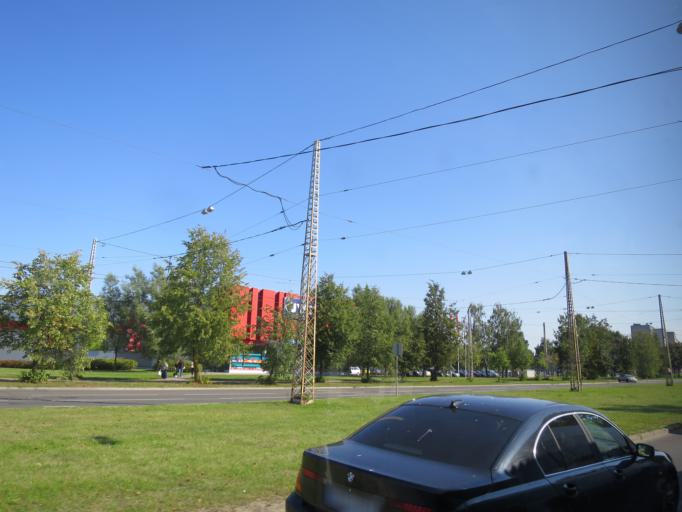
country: LV
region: Riga
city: Riga
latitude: 56.9577
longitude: 24.1847
